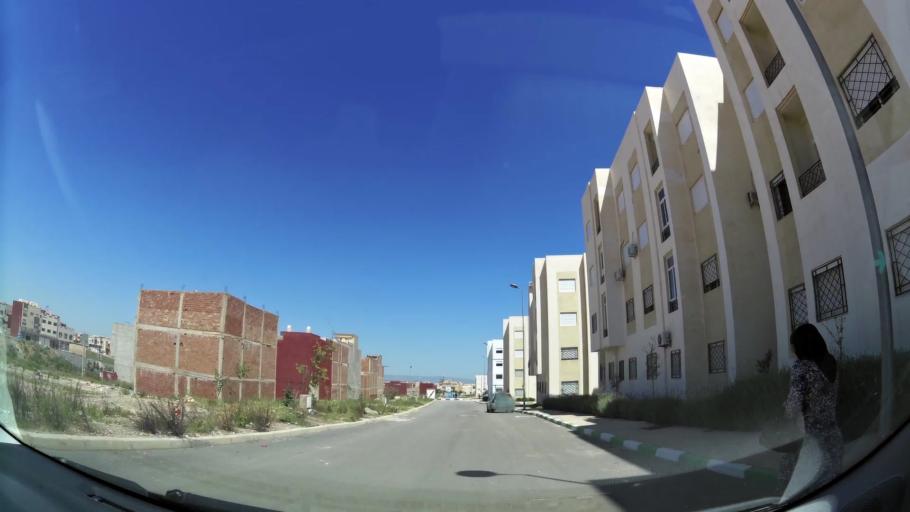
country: MA
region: Oriental
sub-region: Oujda-Angad
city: Oujda
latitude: 34.6532
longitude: -1.8816
